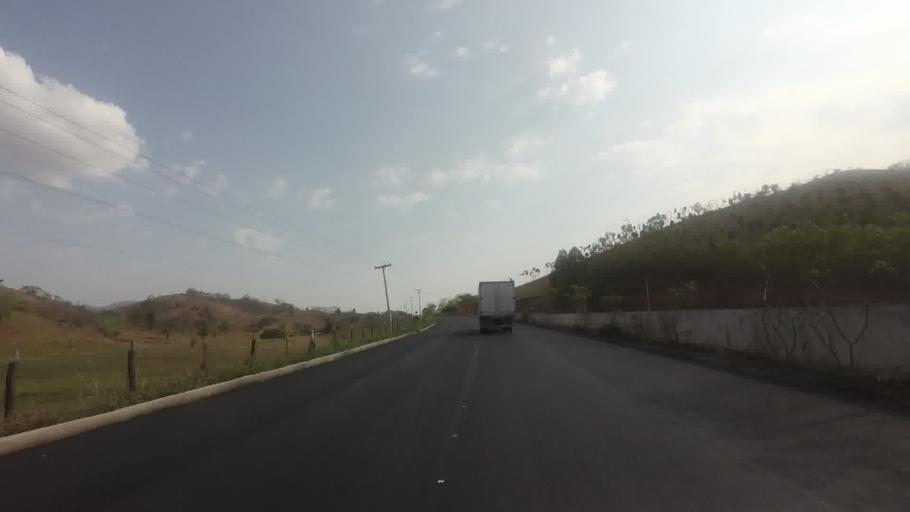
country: BR
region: Rio de Janeiro
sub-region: Bom Jesus Do Itabapoana
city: Bom Jesus do Itabapoana
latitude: -21.1578
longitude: -41.6724
